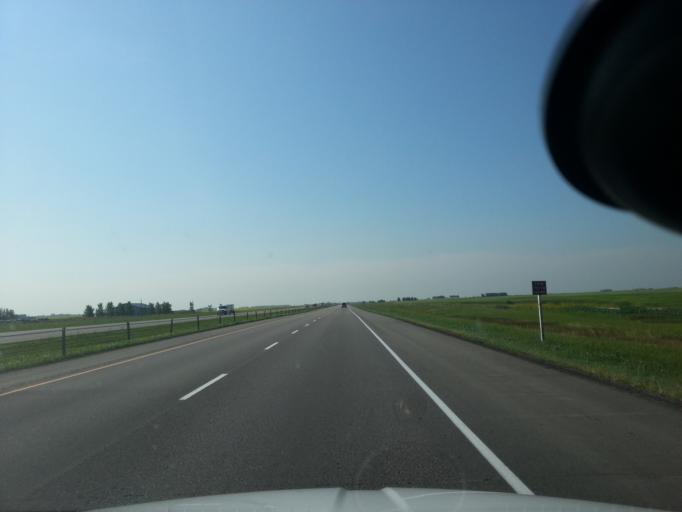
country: CA
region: Alberta
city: Olds
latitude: 51.7045
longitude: -114.0256
